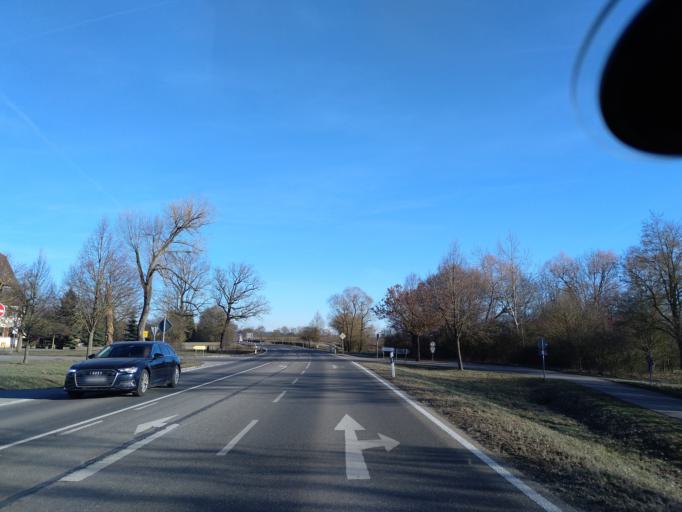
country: DE
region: Baden-Wuerttemberg
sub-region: Regierungsbezirk Stuttgart
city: Vellberg
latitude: 49.0882
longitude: 9.8510
